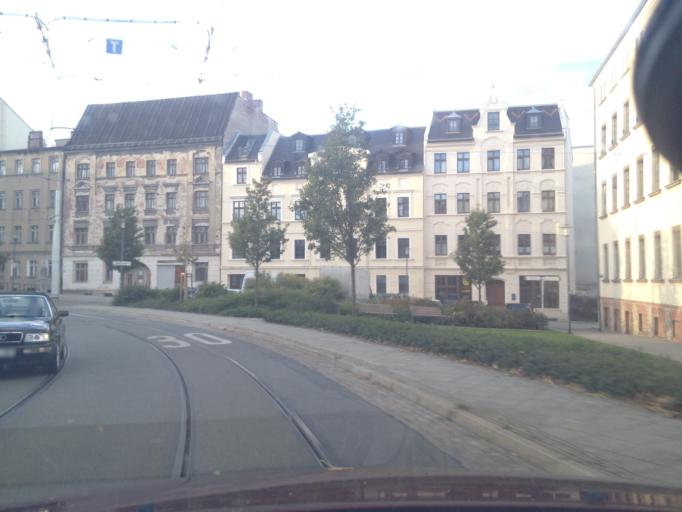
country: DE
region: Saxony
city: Goerlitz
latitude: 51.1583
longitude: 14.9845
